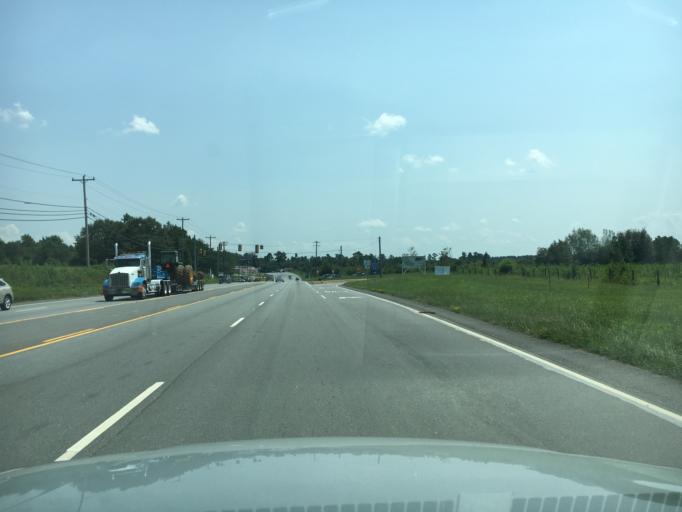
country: US
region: South Carolina
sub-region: Anderson County
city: Pendleton
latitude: 34.6265
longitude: -82.7799
